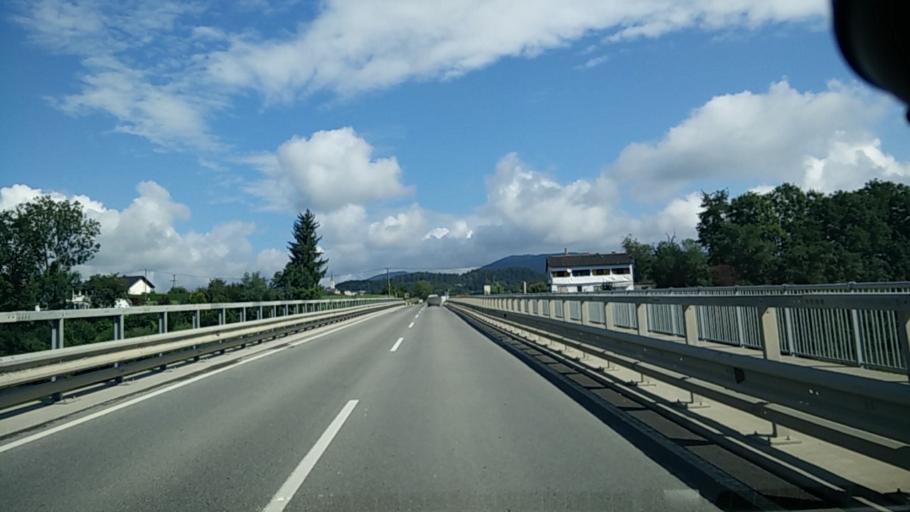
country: AT
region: Carinthia
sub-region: Politischer Bezirk Volkermarkt
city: Gallizien
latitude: 46.6201
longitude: 14.5473
